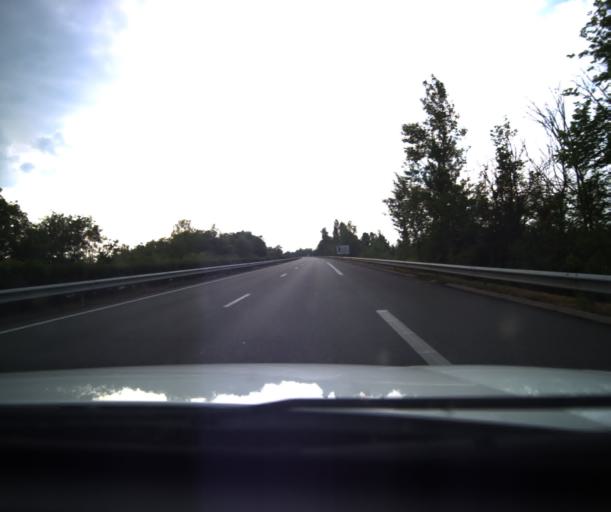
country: FR
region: Midi-Pyrenees
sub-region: Departement du Tarn-et-Garonne
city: Castelsarrasin
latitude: 44.0553
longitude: 1.1241
